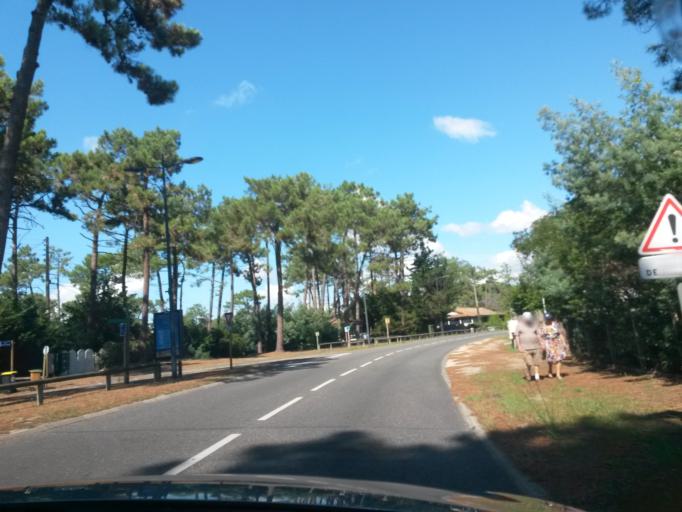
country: FR
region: Aquitaine
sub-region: Departement de la Gironde
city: Arcachon
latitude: 44.7090
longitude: -1.2246
